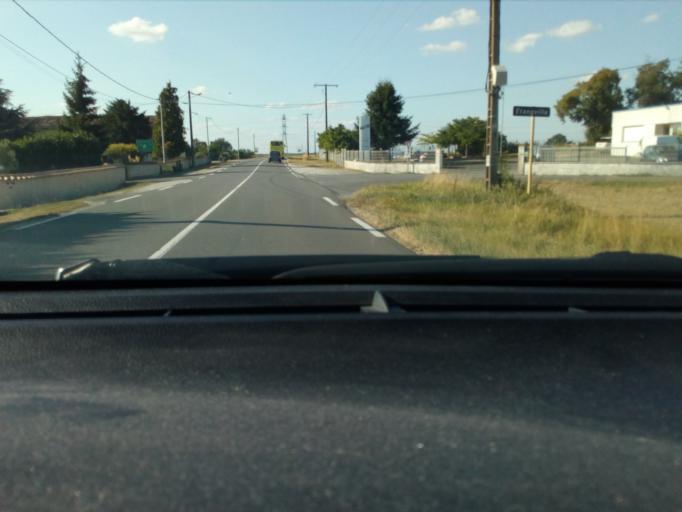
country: FR
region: Poitou-Charentes
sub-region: Departement de la Charente
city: Balzac
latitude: 45.6969
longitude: 0.0977
